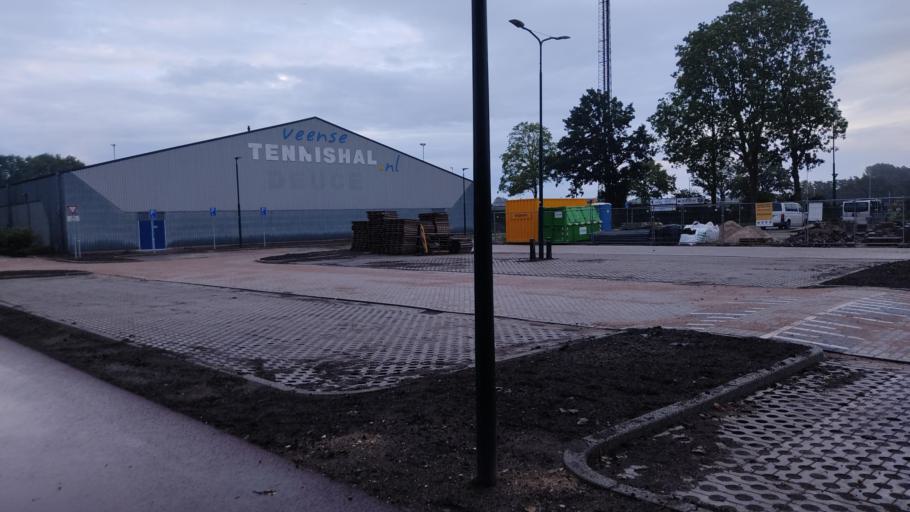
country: NL
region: Utrecht
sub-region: Gemeente Veenendaal
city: Veenendaal
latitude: 52.0291
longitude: 5.5746
